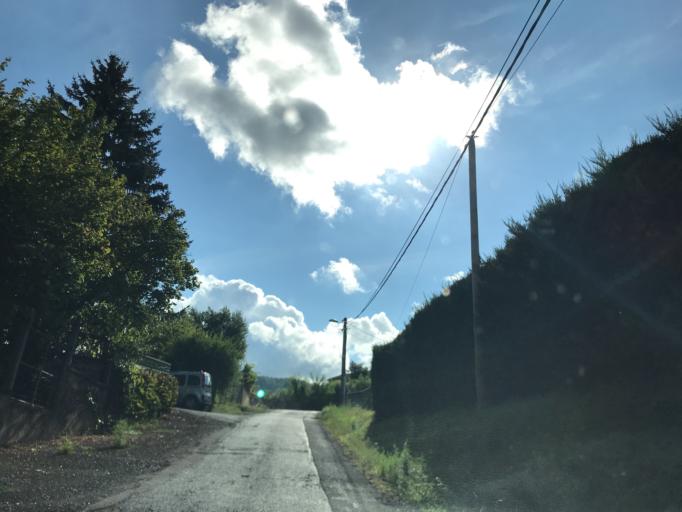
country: FR
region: Auvergne
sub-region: Departement du Puy-de-Dome
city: Thiers
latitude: 45.8443
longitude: 3.5358
